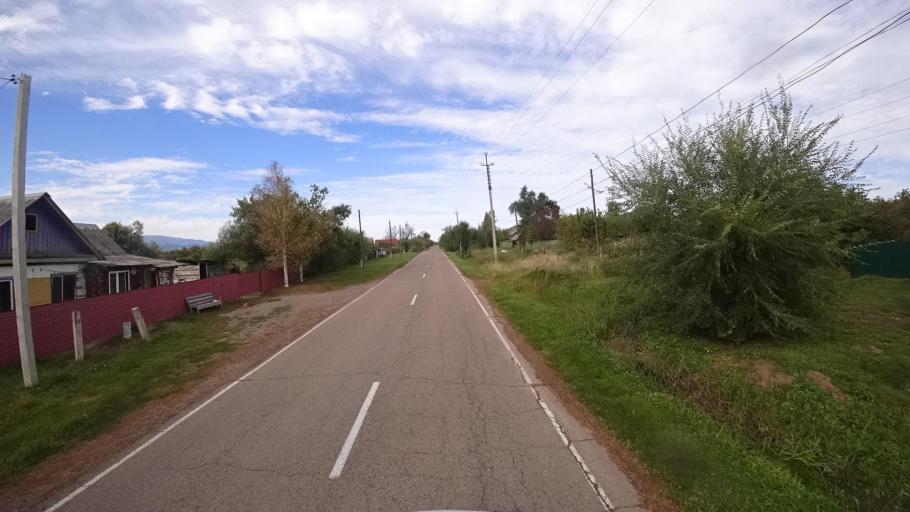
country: RU
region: Primorskiy
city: Dostoyevka
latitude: 44.3221
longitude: 133.4763
